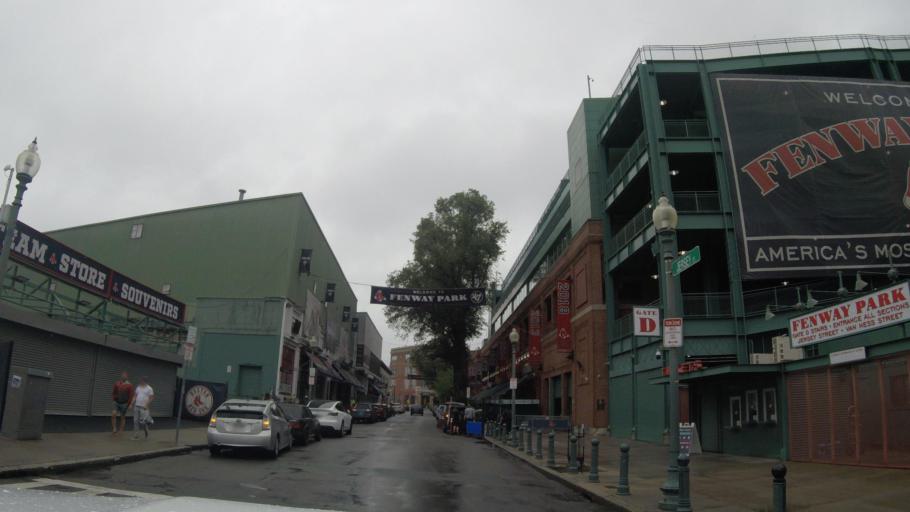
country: US
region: Massachusetts
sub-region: Norfolk County
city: Brookline
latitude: 42.3454
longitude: -71.0982
